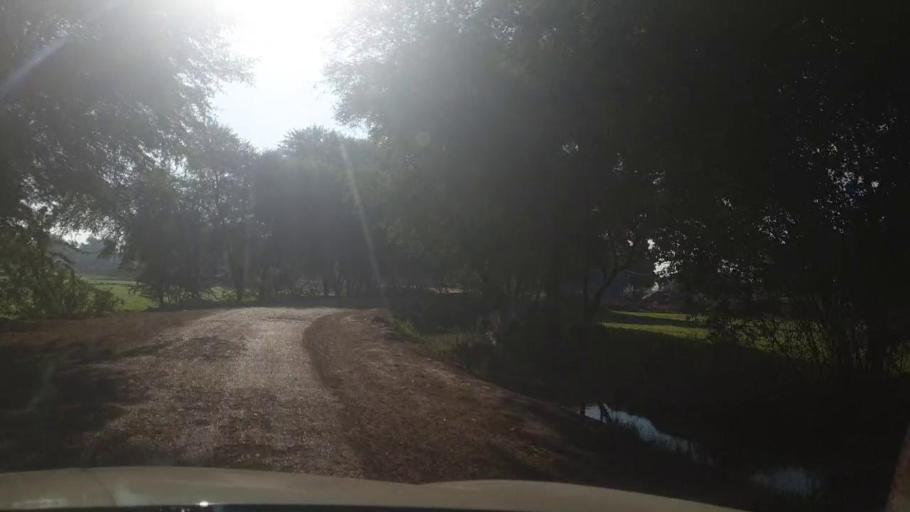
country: PK
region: Sindh
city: Bhan
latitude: 26.5448
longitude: 67.6762
